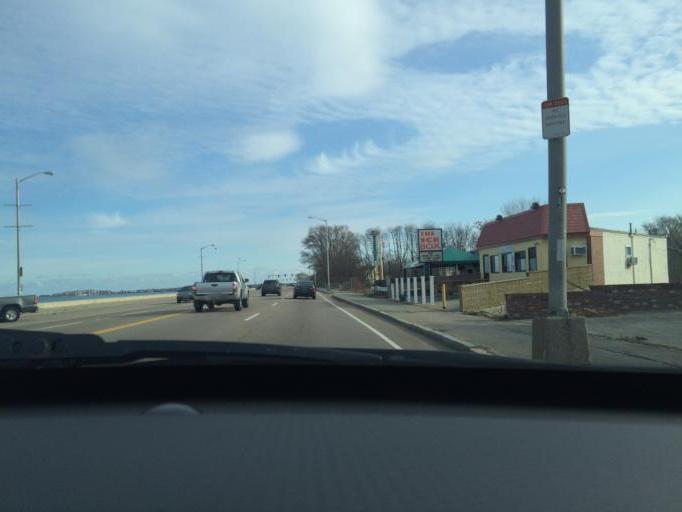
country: US
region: Massachusetts
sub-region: Norfolk County
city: Quincy
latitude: 42.2766
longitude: -71.0095
